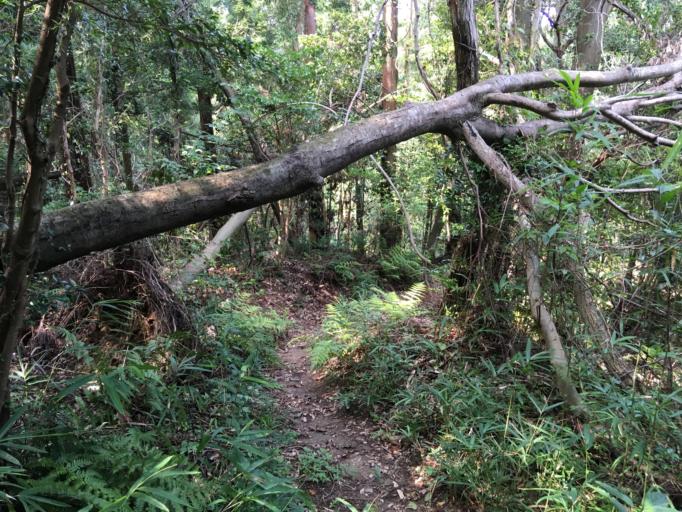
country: JP
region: Nara
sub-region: Ikoma-shi
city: Ikoma
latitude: 34.6976
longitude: 135.6846
